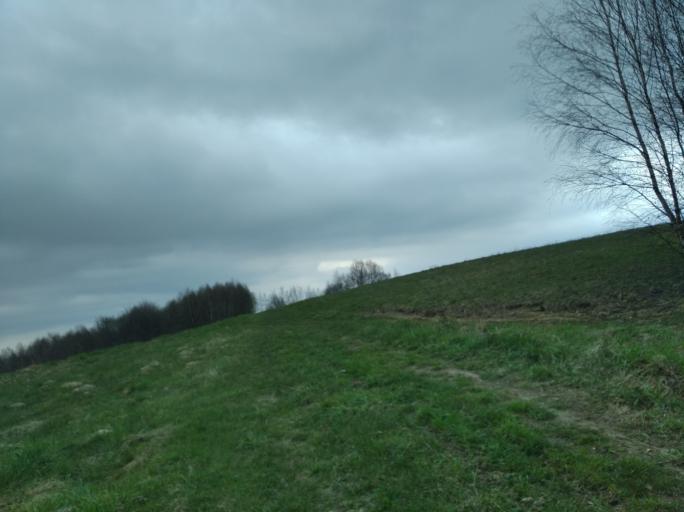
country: PL
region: Subcarpathian Voivodeship
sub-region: Powiat strzyzowski
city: Jawornik
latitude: 49.8152
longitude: 21.9024
